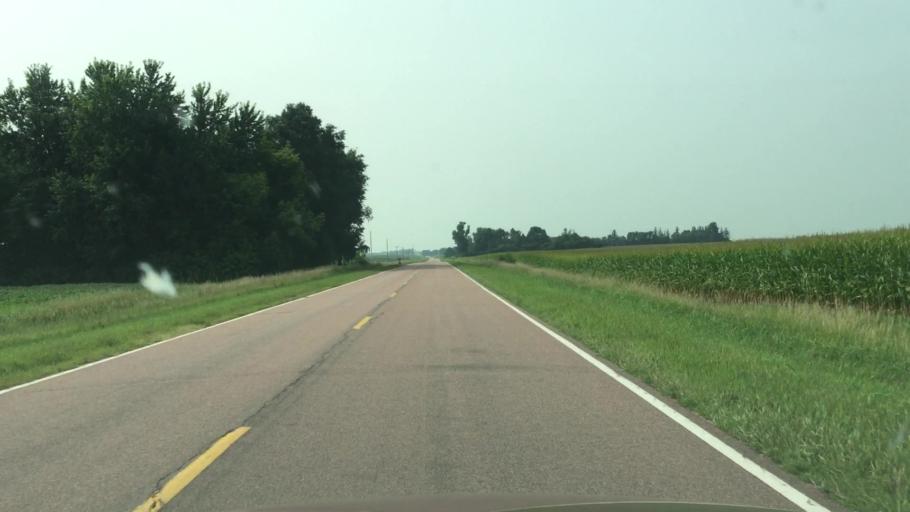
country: US
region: Iowa
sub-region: O'Brien County
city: Sheldon
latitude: 43.2541
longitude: -95.7831
